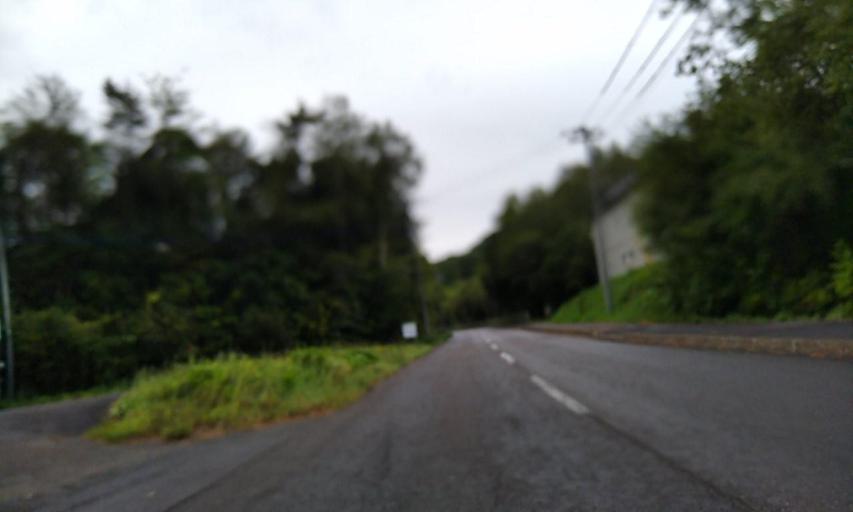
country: JP
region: Hokkaido
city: Abashiri
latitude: 44.0020
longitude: 144.2309
